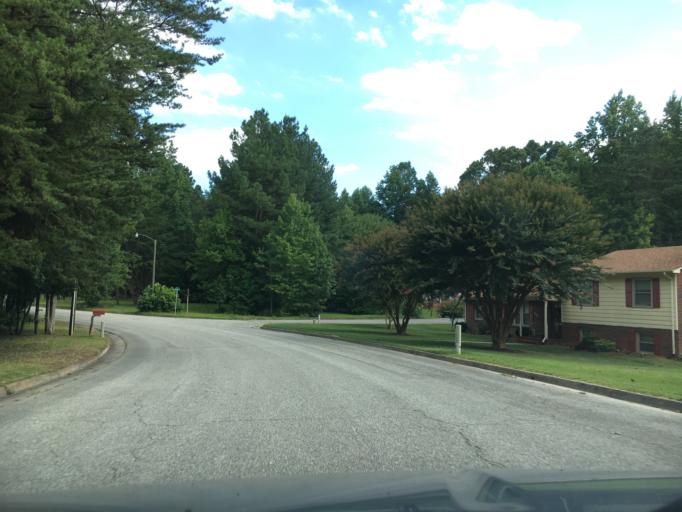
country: US
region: Virginia
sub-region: Halifax County
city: South Boston
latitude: 36.7171
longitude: -78.9055
